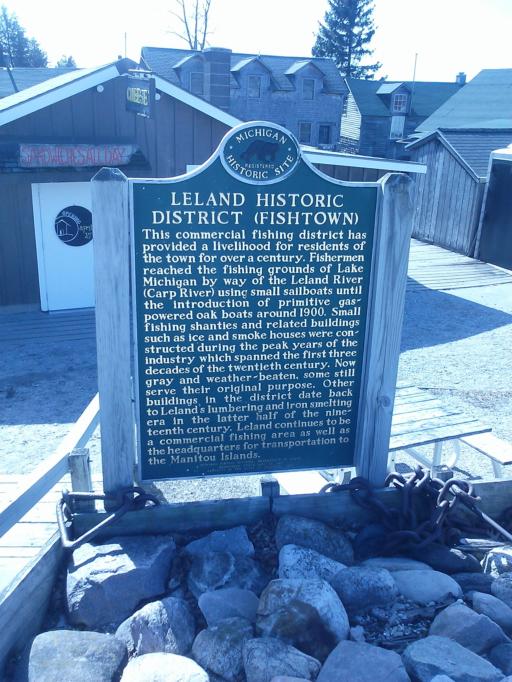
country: US
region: Michigan
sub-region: Leelanau County
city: Leland
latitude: 45.0235
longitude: -85.7615
